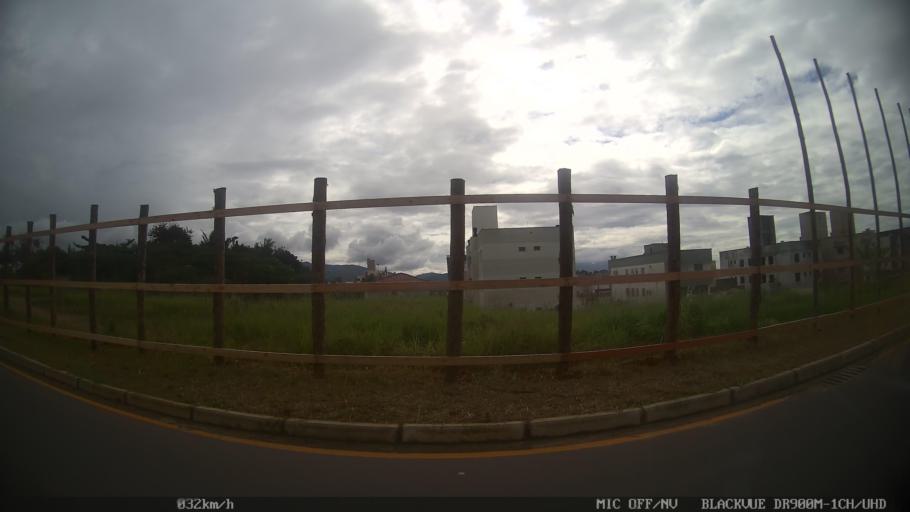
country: BR
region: Santa Catarina
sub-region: Sao Jose
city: Campinas
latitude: -27.5462
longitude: -48.6296
